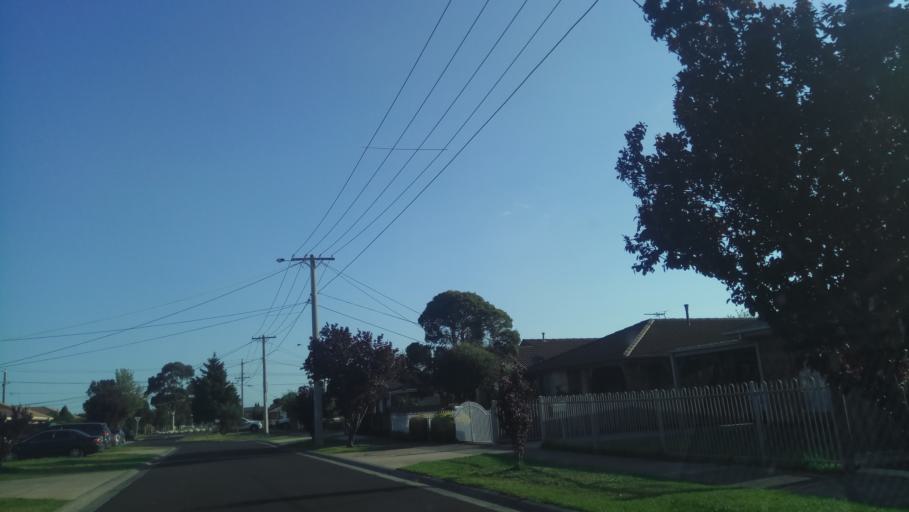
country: AU
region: Victoria
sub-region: Hobsons Bay
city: Altona Meadows
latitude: -37.8737
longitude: 144.7840
